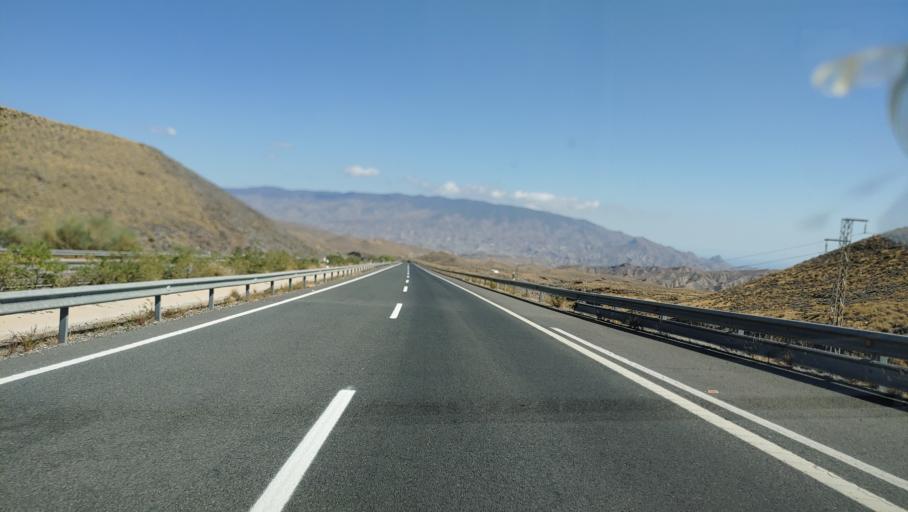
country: ES
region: Andalusia
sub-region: Provincia de Almeria
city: Gergal
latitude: 37.0874
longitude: -2.5205
